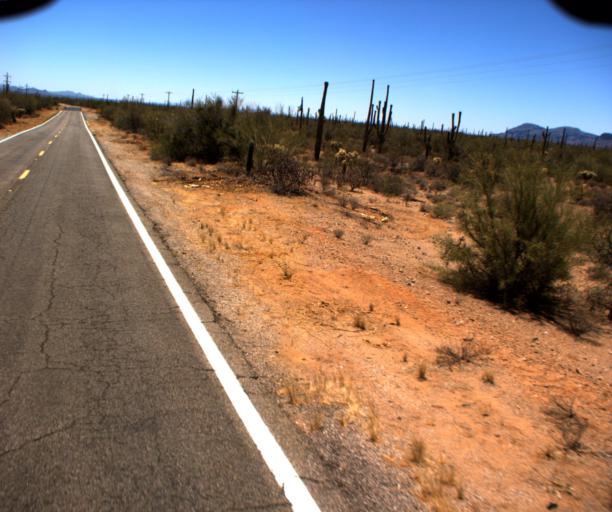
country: US
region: Arizona
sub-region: Pima County
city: Sells
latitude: 32.1458
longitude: -112.1018
